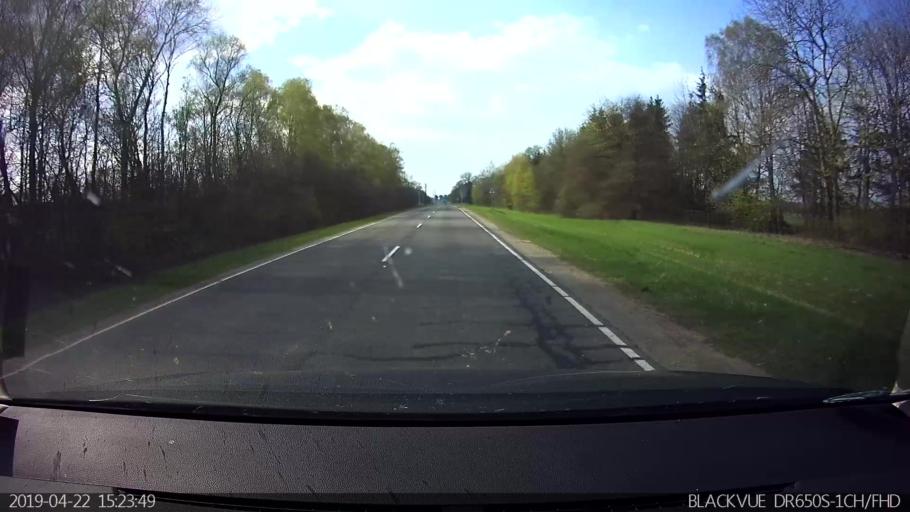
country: BY
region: Brest
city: Vysokaye
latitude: 52.3575
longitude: 23.4190
